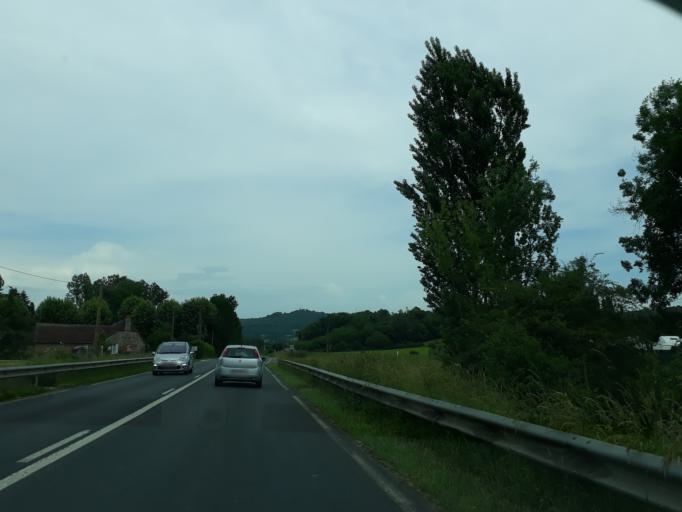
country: FR
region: Limousin
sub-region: Departement de la Correze
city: Larche
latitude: 45.1253
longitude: 1.3956
